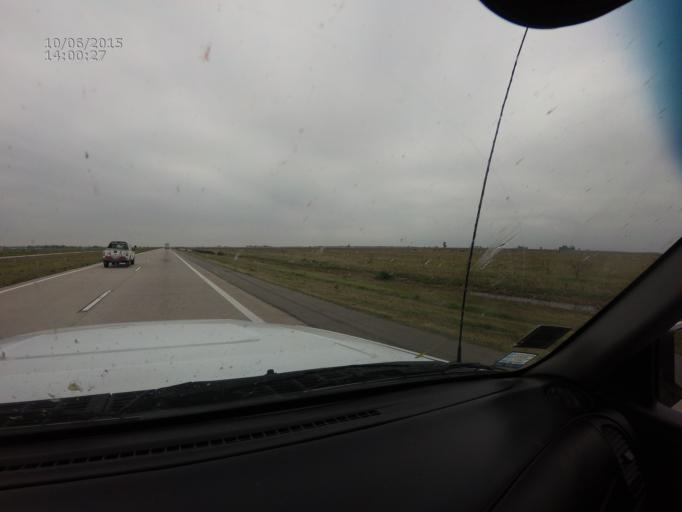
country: AR
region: Cordoba
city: Morrison
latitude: -32.5407
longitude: -62.8911
